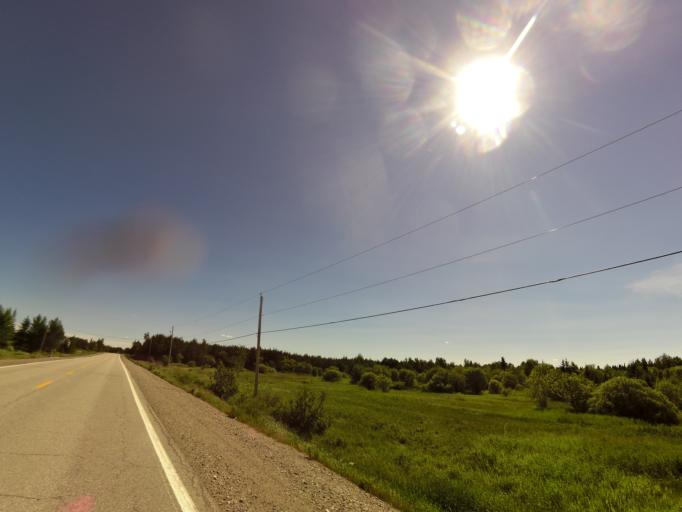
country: CA
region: Quebec
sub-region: Abitibi-Temiscamingue
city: Senneterre
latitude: 48.2862
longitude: -77.3121
